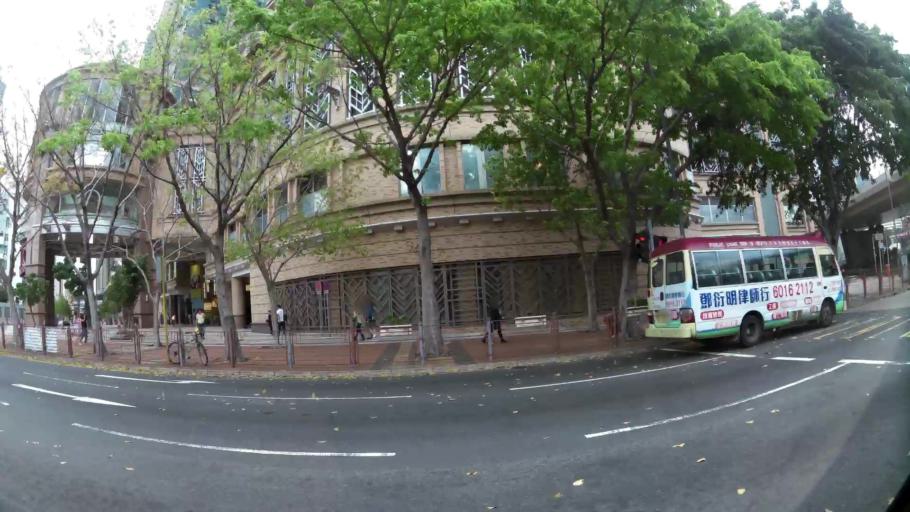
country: HK
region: Sham Shui Po
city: Sham Shui Po
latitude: 22.3340
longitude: 114.1502
